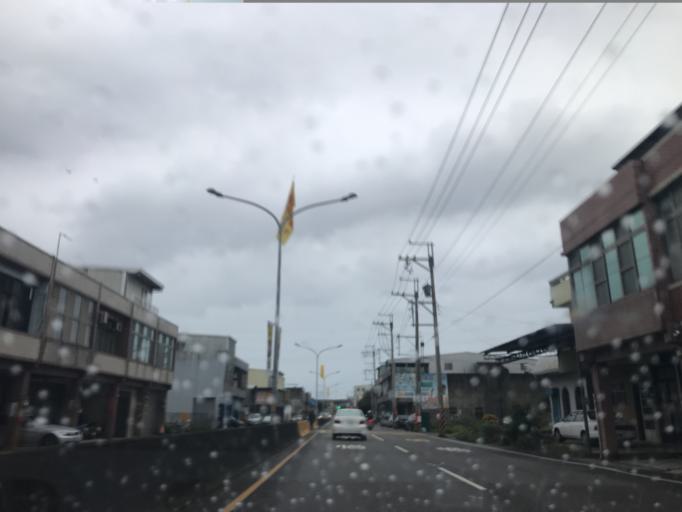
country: TW
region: Taiwan
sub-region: Hsinchu
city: Zhubei
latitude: 24.8265
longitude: 121.0523
